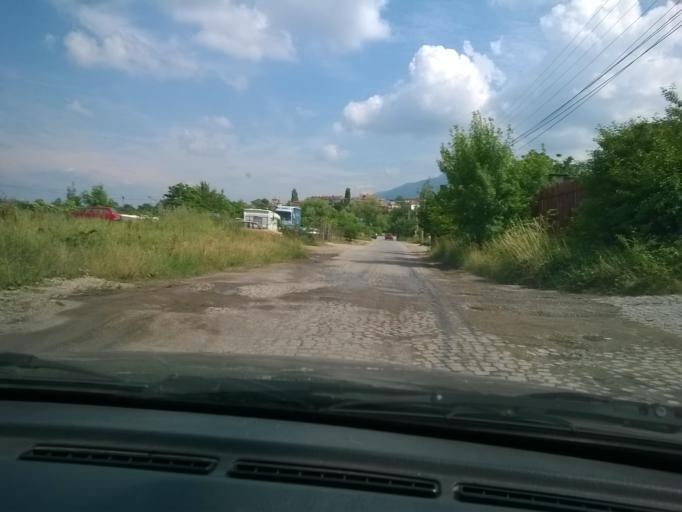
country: BG
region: Sofiya
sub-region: Obshtina Bozhurishte
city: Bozhurishte
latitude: 42.6851
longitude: 23.2355
